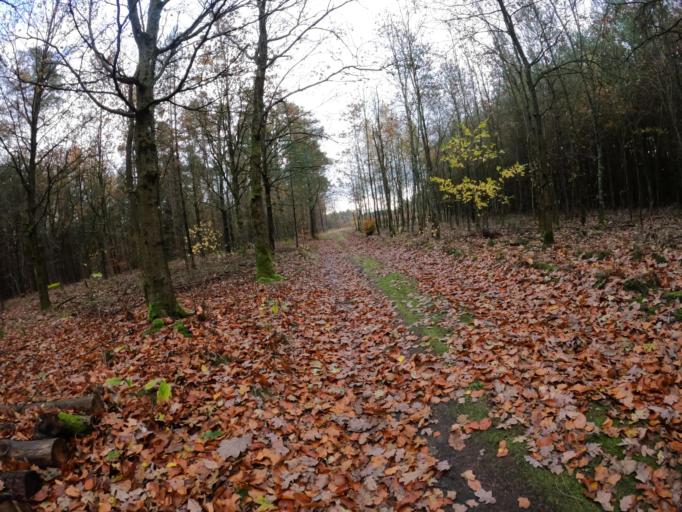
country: PL
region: West Pomeranian Voivodeship
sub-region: Powiat walecki
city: Tuczno
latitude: 53.2299
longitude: 16.2674
